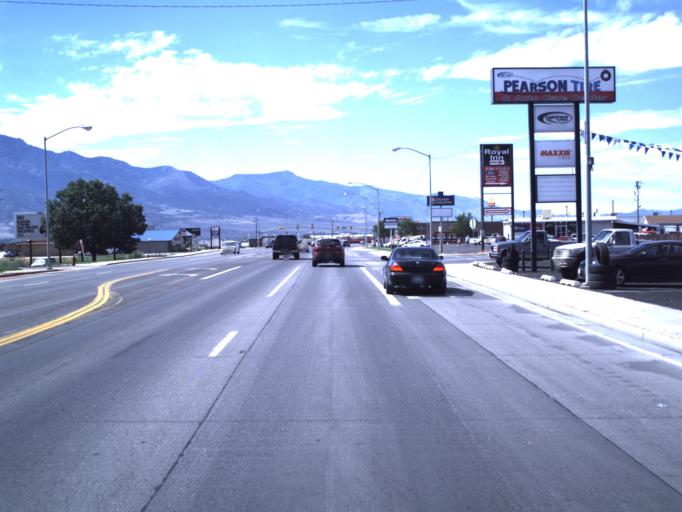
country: US
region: Utah
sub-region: Sevier County
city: Richfield
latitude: 38.7597
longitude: -112.0849
